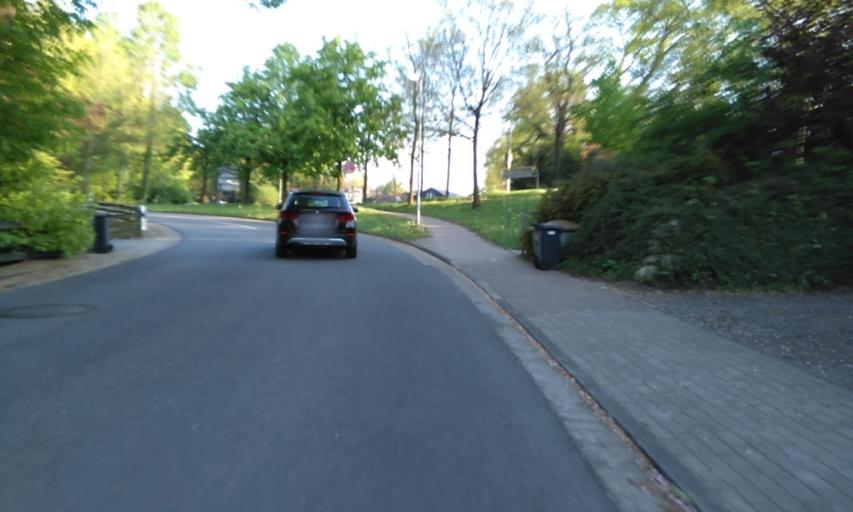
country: DE
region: Lower Saxony
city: Dollern
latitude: 53.5372
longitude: 9.5481
